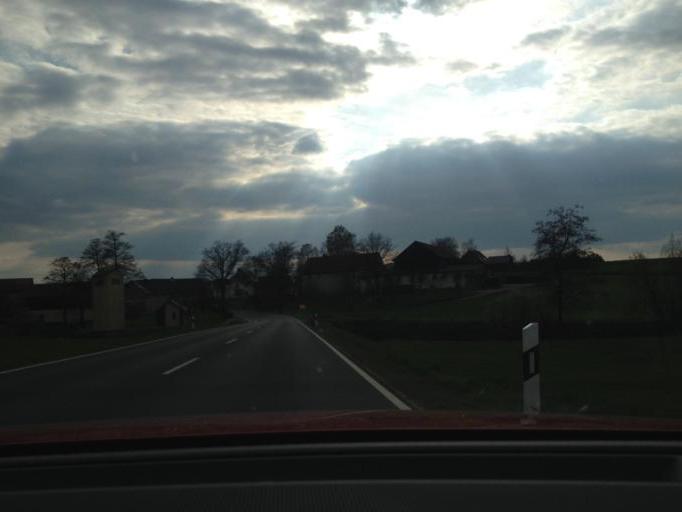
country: DE
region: Bavaria
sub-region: Upper Palatinate
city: Kemnath
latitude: 49.8558
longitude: 11.8707
